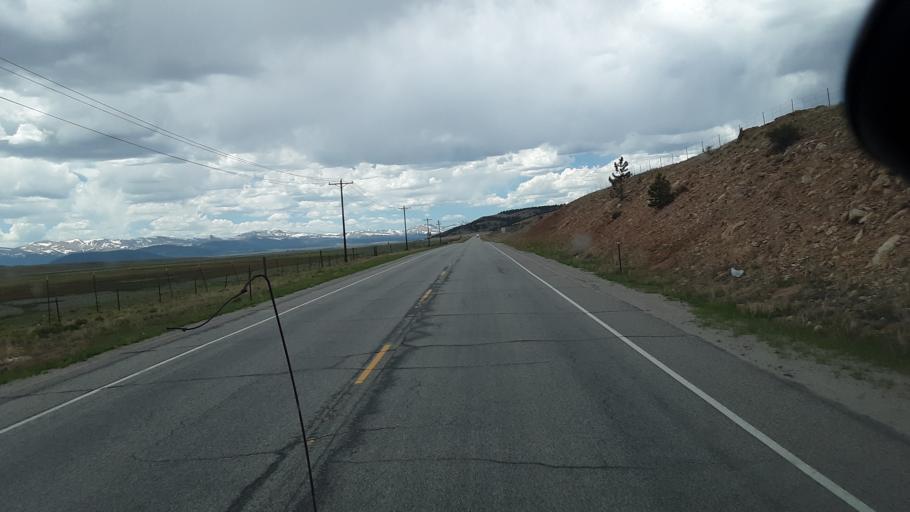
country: US
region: Colorado
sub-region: Park County
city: Fairplay
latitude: 39.0274
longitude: -105.8166
